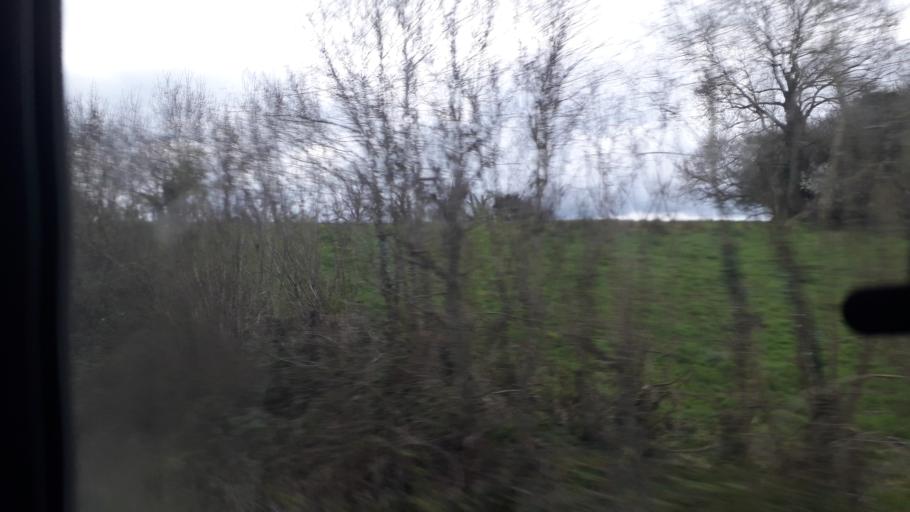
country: IE
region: Leinster
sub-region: An Longfort
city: Longford
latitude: 53.7430
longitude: -7.8228
